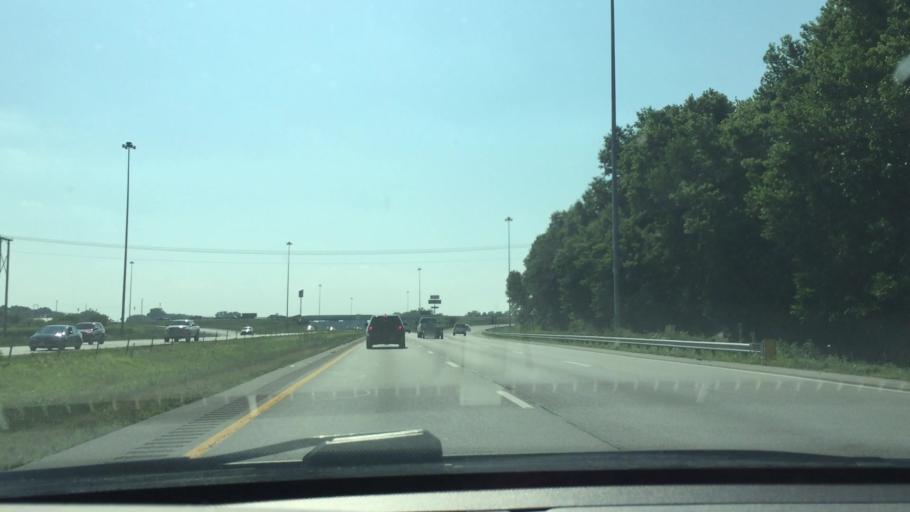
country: US
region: Ohio
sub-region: Fairfield County
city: Millersport
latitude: 39.9422
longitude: -82.5301
